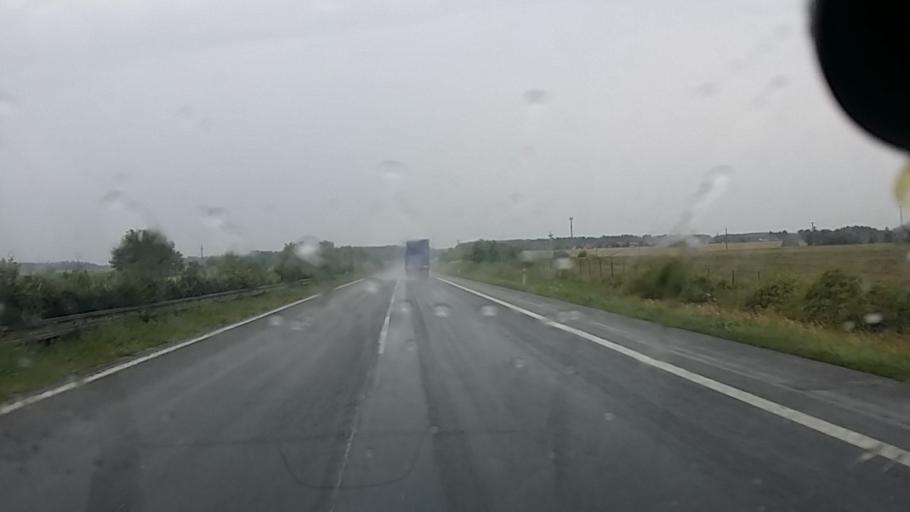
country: AT
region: Lower Austria
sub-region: Politischer Bezirk Mistelbach
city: Rabensburg
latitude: 48.5981
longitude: 17.0159
